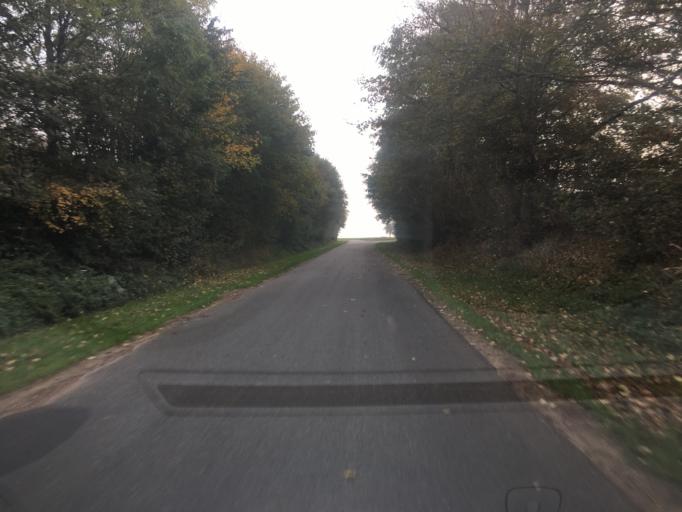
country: DK
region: South Denmark
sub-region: Tonder Kommune
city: Toftlund
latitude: 55.1038
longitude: 9.0842
